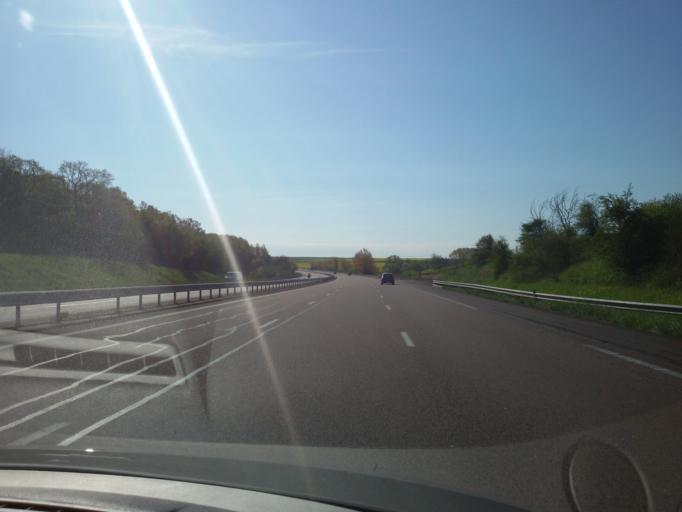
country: FR
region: Bourgogne
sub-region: Departement de l'Yonne
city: Aillant-sur-Tholon
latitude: 47.9037
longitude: 3.3469
